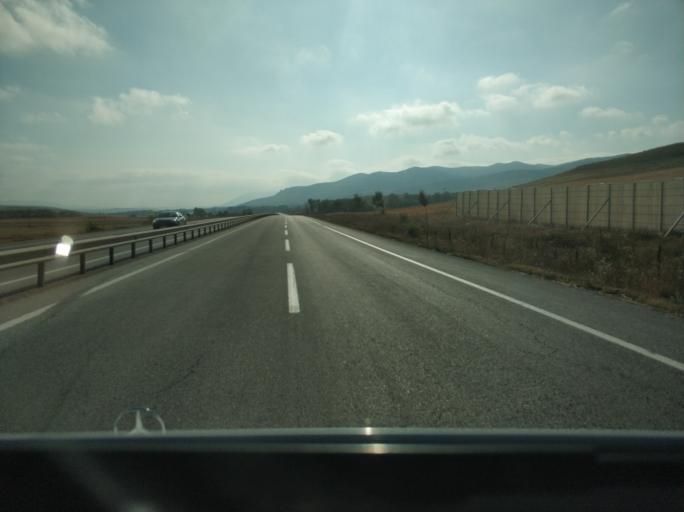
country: TR
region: Sivas
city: Yildizeli
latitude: 39.8355
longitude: 36.4361
